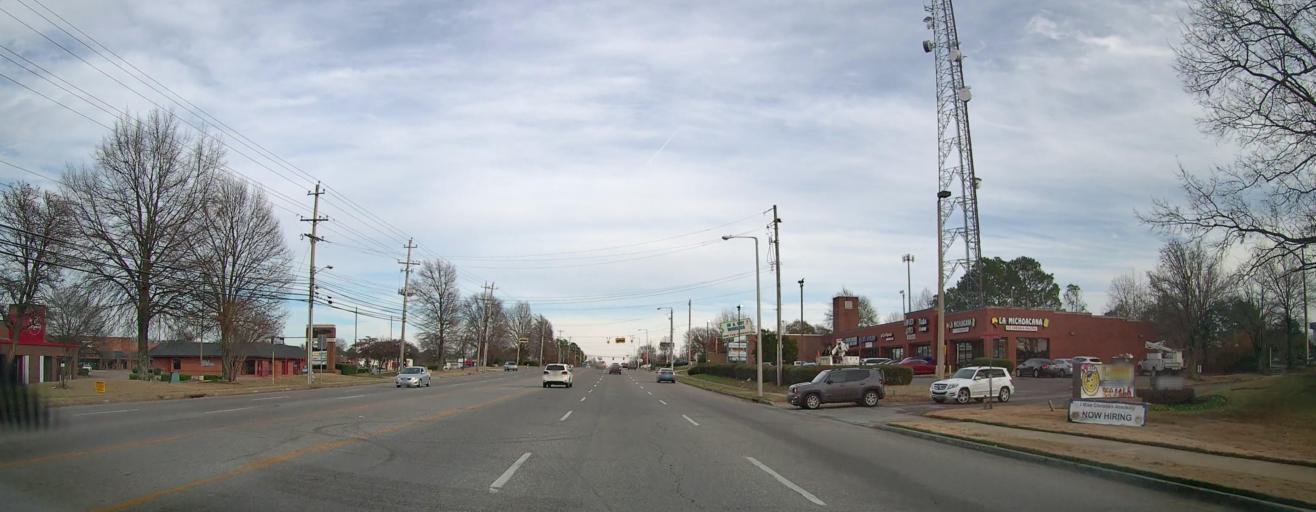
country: US
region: Tennessee
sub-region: Shelby County
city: Germantown
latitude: 35.0496
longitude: -89.8432
